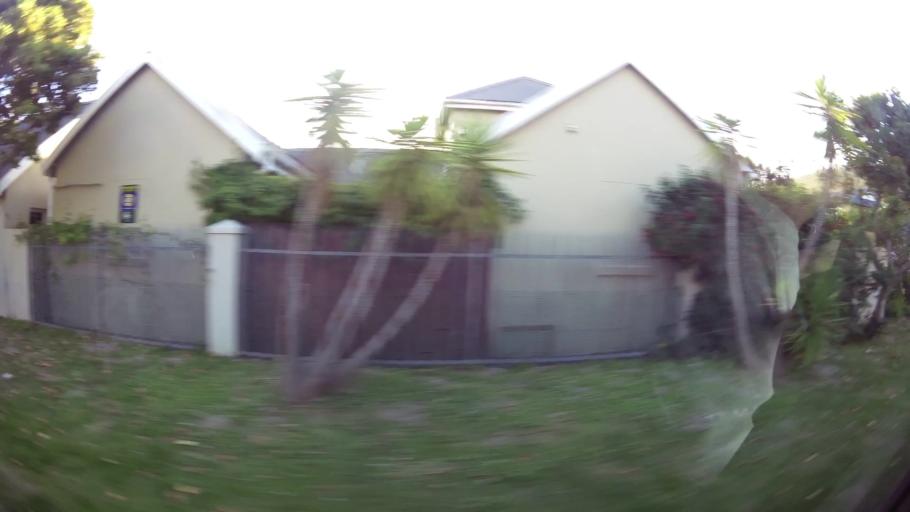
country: ZA
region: Western Cape
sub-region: Eden District Municipality
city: Knysna
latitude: -34.0119
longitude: 22.7945
